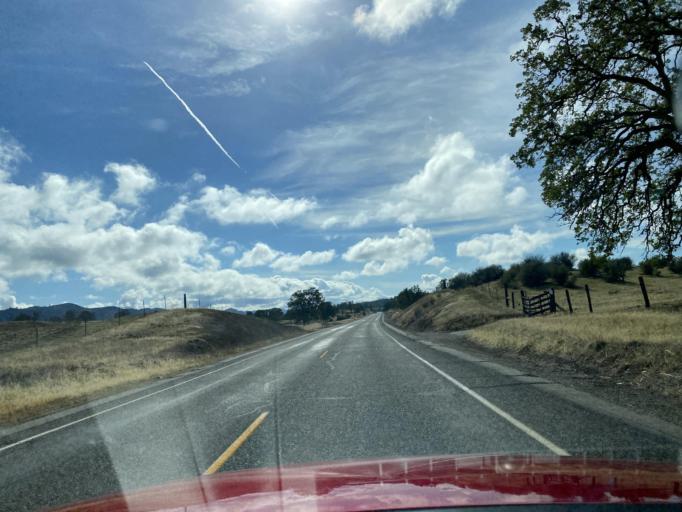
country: US
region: California
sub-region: Glenn County
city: Willows
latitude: 39.5137
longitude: -122.5276
